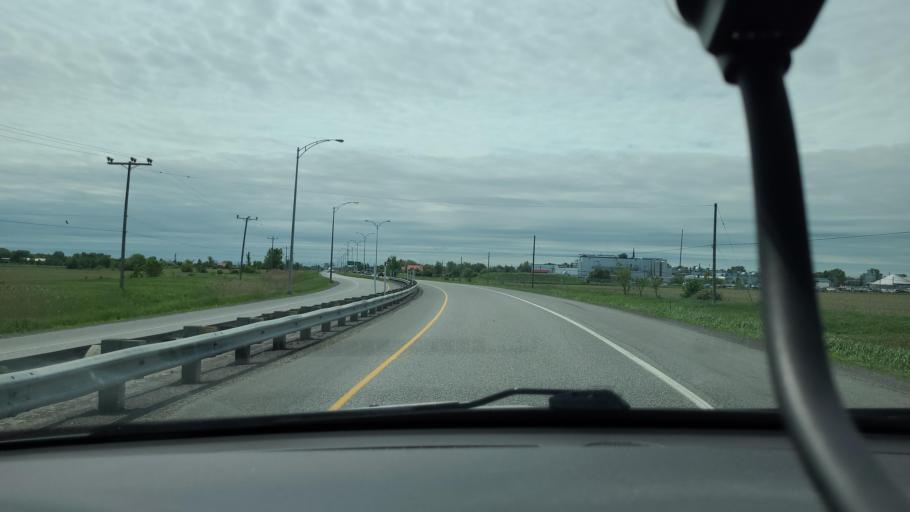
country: CA
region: Quebec
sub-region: Lanaudiere
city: Sainte-Julienne
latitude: 45.9104
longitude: -73.6580
